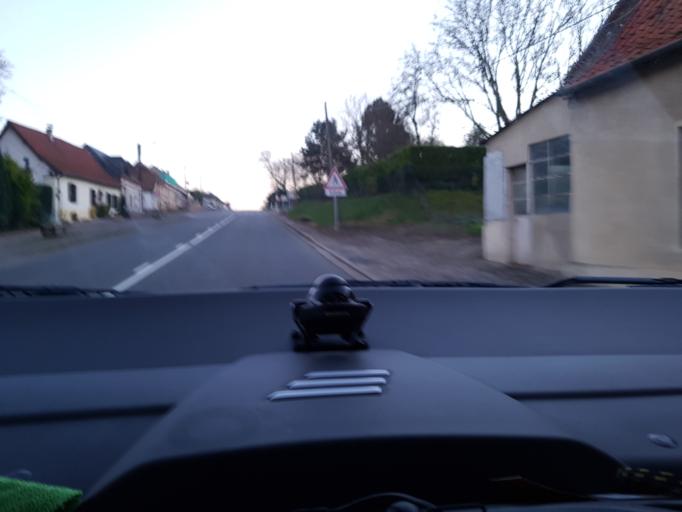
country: FR
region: Picardie
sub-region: Departement de la Somme
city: Rue
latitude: 50.3133
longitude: 1.7505
